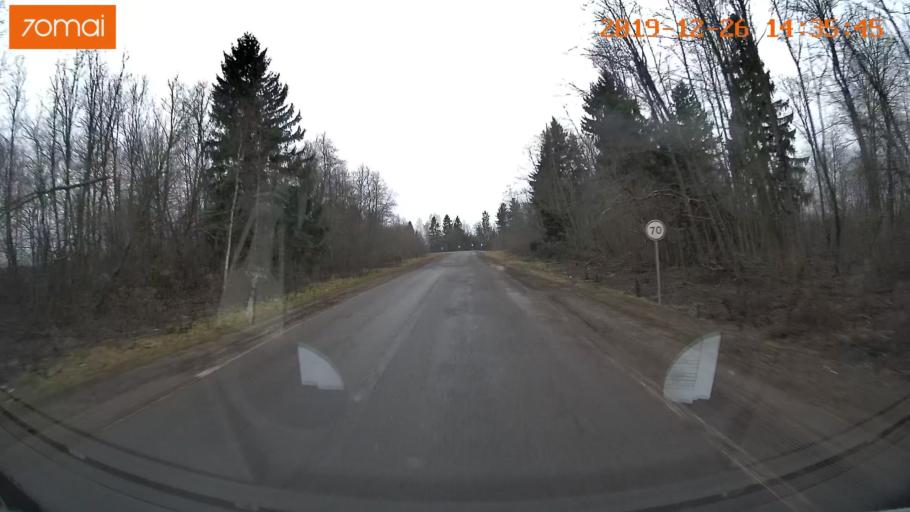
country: RU
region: Jaroslavl
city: Poshekhon'ye
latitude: 58.4175
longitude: 38.9804
